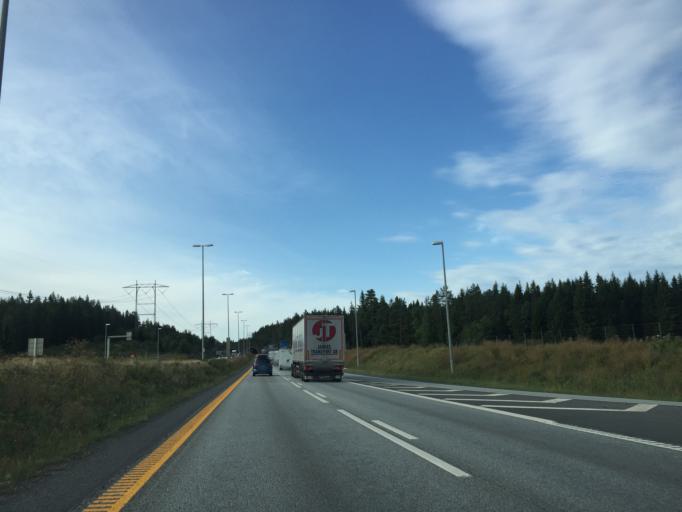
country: NO
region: Akershus
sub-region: Oppegard
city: Kolbotn
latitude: 59.7949
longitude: 10.8420
